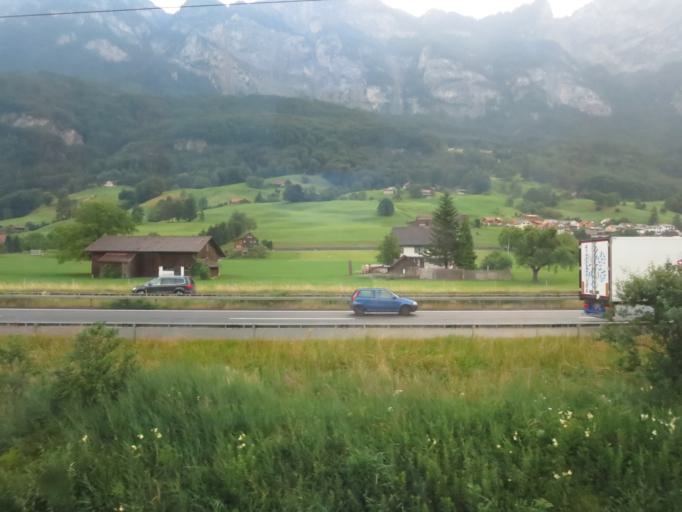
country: CH
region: Saint Gallen
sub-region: Wahlkreis Sarganserland
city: Flums
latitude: 47.0835
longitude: 9.3651
